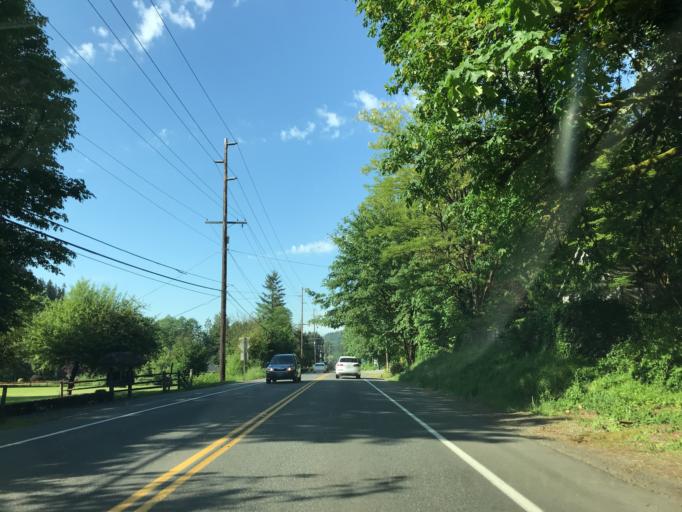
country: US
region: Washington
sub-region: King County
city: Mirrormont
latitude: 47.4875
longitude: -122.0258
